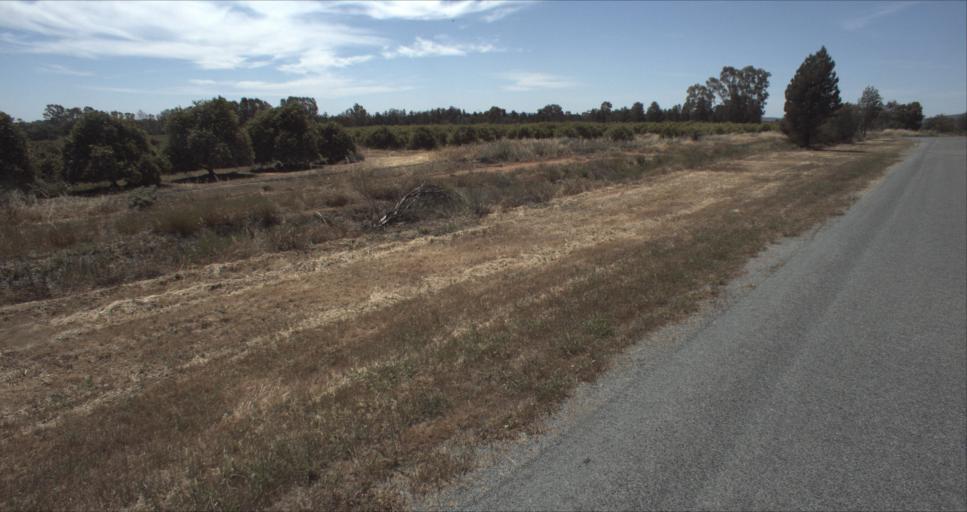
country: AU
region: New South Wales
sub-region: Leeton
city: Leeton
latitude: -34.5763
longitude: 146.4338
